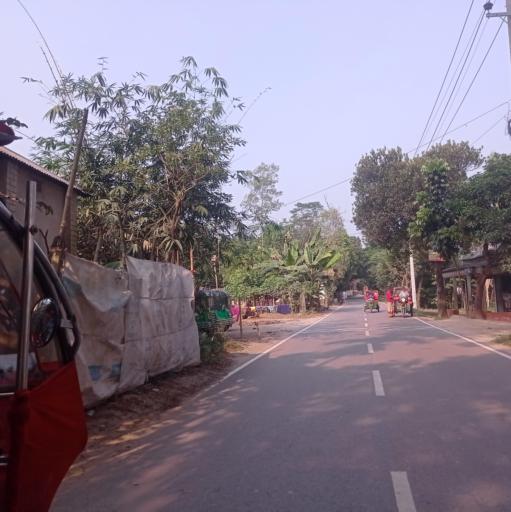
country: BD
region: Dhaka
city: Bhairab Bazar
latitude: 24.0921
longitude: 90.8503
